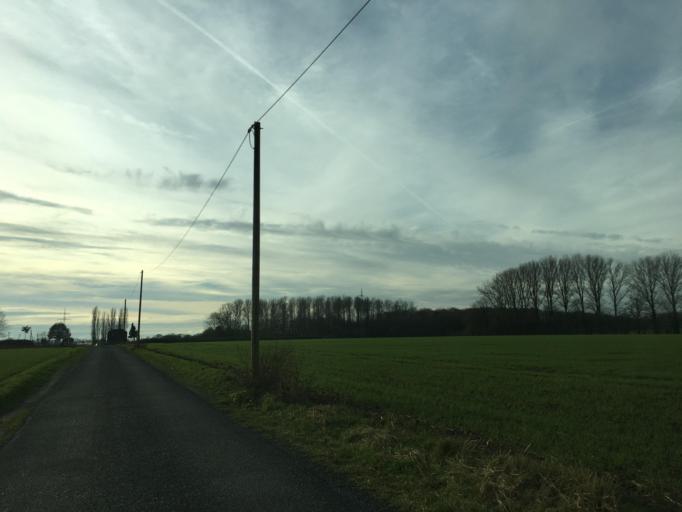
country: DE
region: North Rhine-Westphalia
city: Ludinghausen
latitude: 51.8007
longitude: 7.3708
